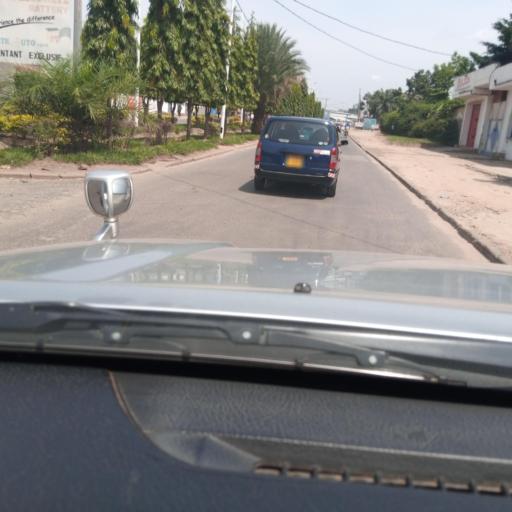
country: BI
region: Bujumbura Mairie
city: Bujumbura
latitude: -3.3757
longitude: 29.3514
